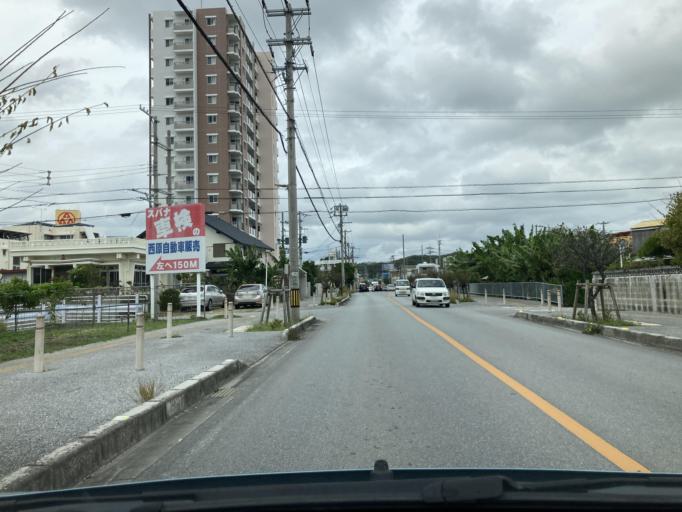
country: JP
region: Okinawa
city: Ginowan
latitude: 26.2246
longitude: 127.7676
